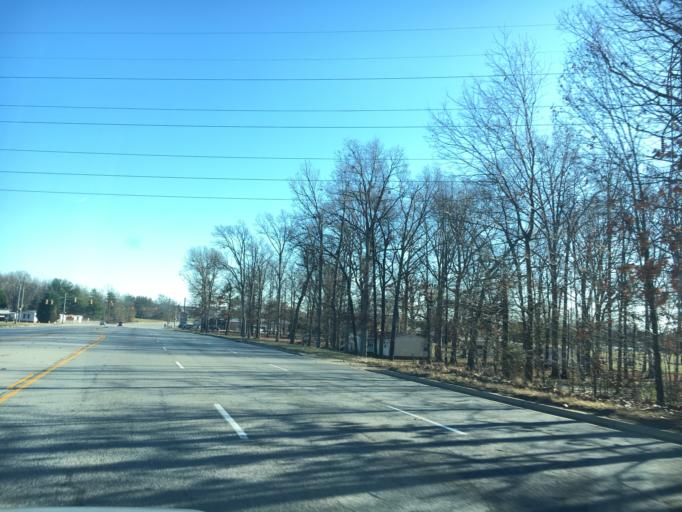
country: US
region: South Carolina
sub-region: Greenville County
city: Greer
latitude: 34.9035
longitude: -82.2388
